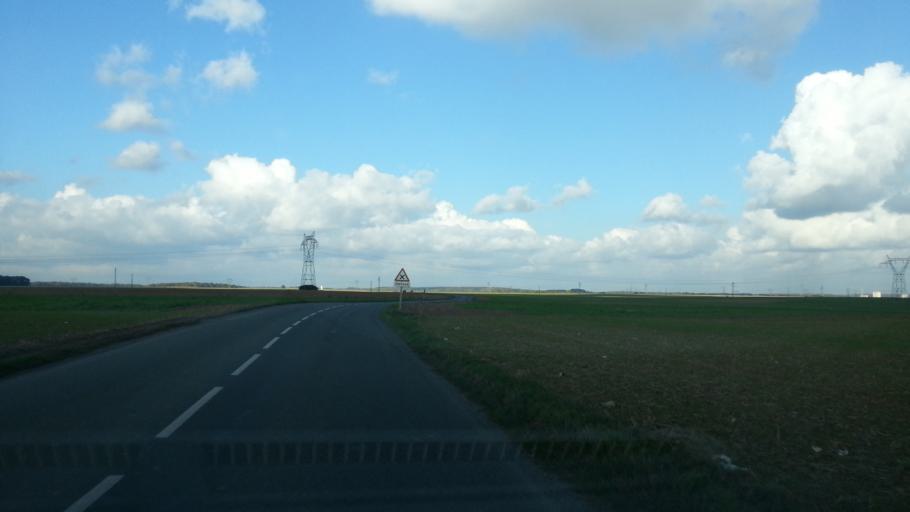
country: FR
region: Picardie
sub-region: Departement de l'Oise
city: Villers-sous-Saint-Leu
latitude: 49.2272
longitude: 2.4139
